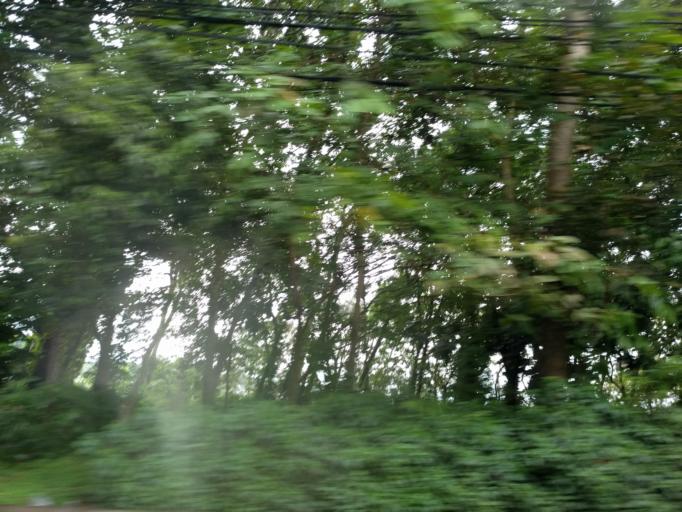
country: ID
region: West Java
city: Bogor
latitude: -6.5903
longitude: 106.8017
